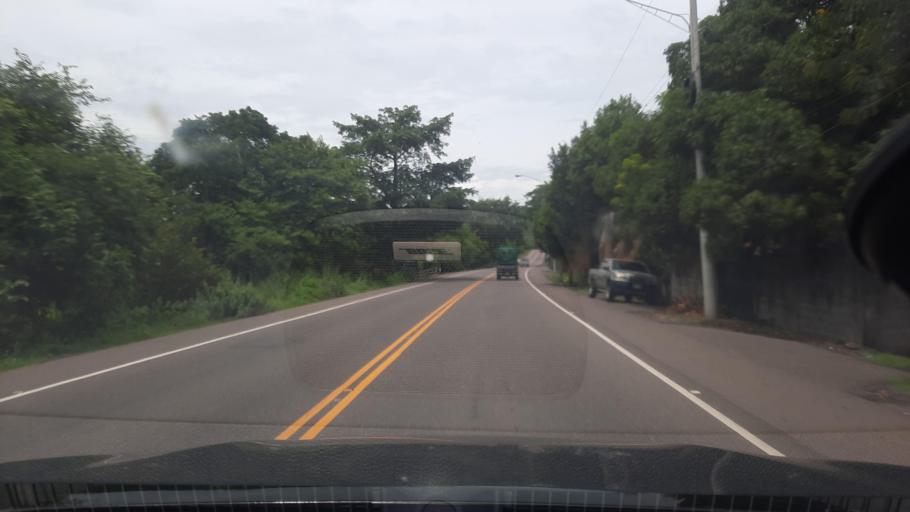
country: HN
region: Valle
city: Goascoran
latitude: 13.5577
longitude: -87.6559
